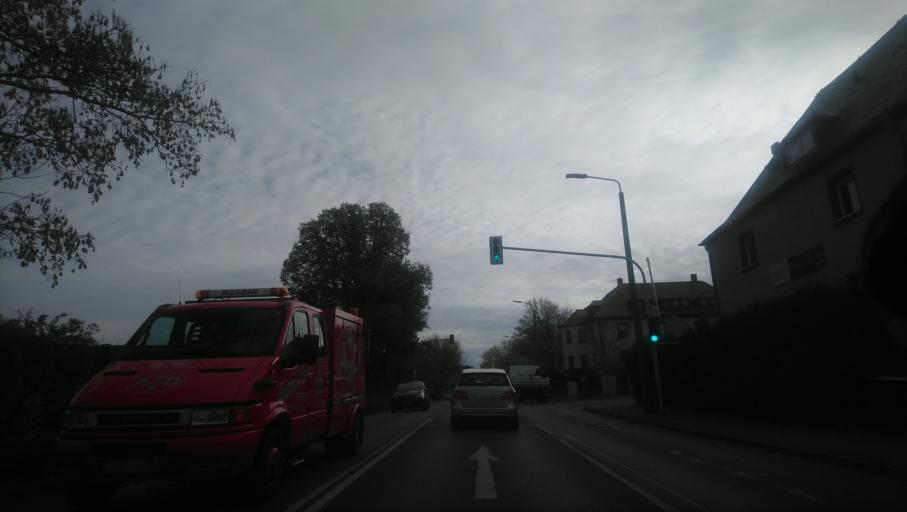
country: DE
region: Saxony
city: Wilkau-Hasslau
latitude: 50.7012
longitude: 12.5137
